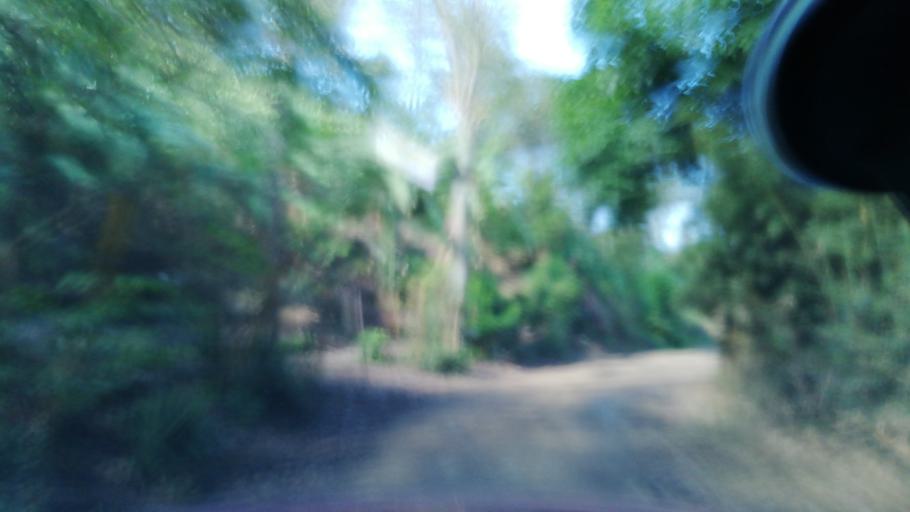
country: CO
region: Cundinamarca
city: Quipile
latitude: 4.7672
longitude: -74.6159
